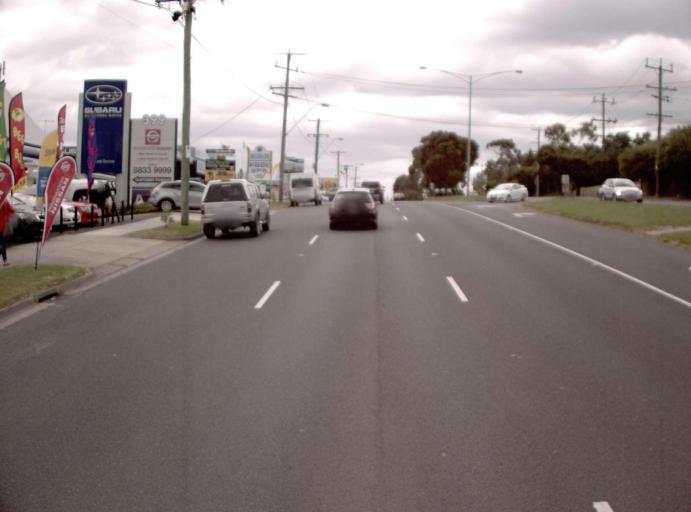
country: AU
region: Victoria
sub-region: Maroondah
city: Ringwood East
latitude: -37.8033
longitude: 145.2467
